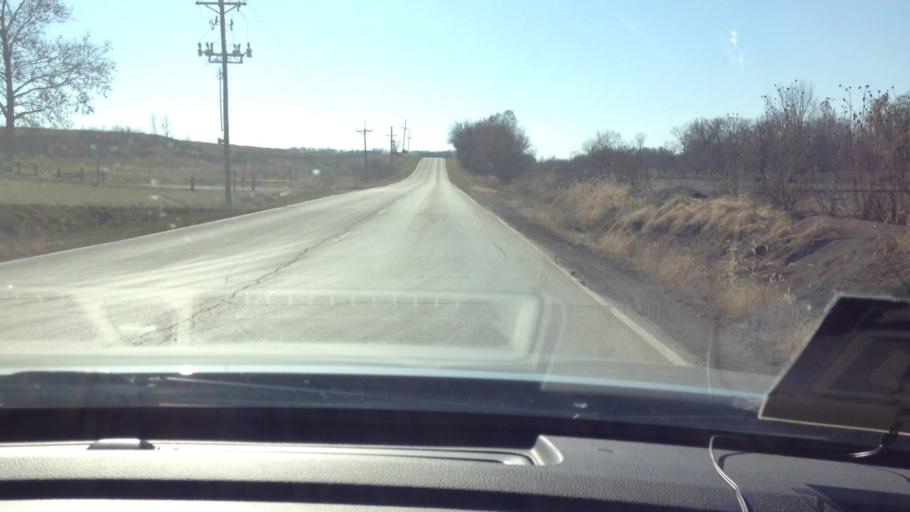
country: US
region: Missouri
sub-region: Platte County
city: Platte City
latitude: 39.4928
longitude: -94.8033
